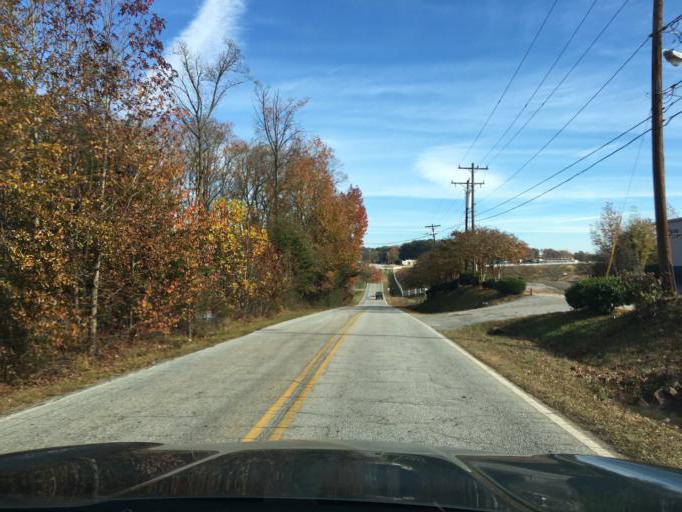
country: US
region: South Carolina
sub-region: Greenville County
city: Greenville
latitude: 34.8562
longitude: -82.3515
